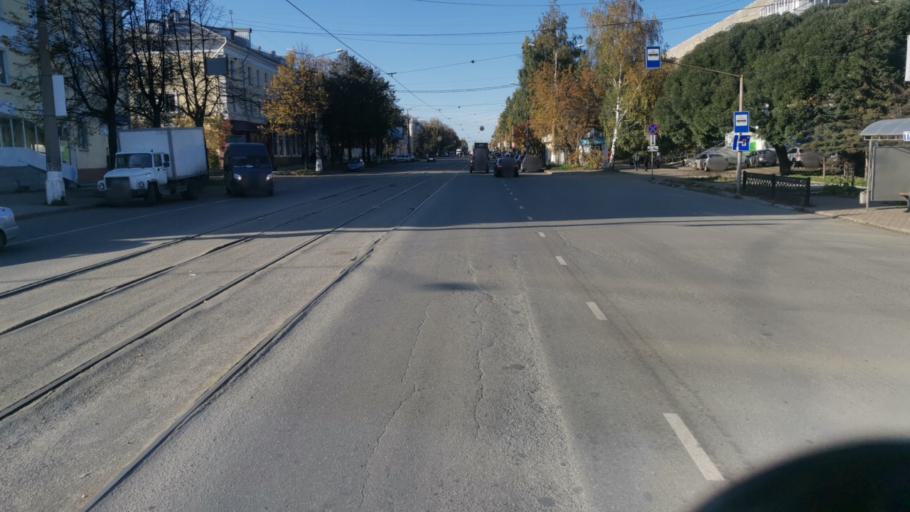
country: RU
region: Sverdlovsk
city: Nizhniy Tagil
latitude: 57.9185
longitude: 59.9440
